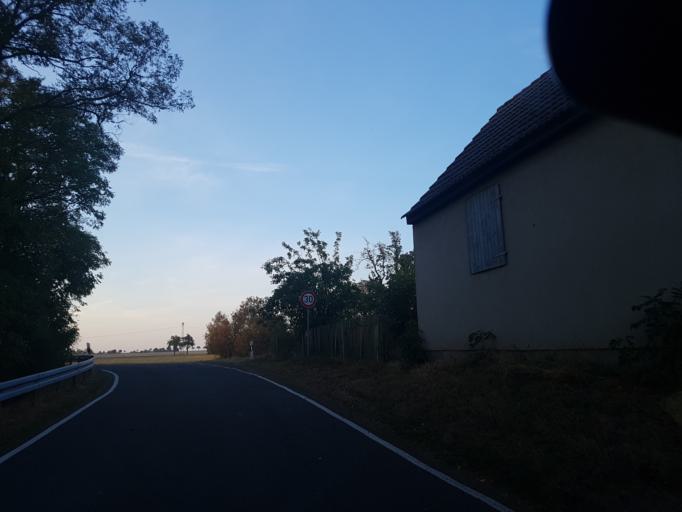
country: DE
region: Saxony
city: Stauchitz
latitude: 51.2898
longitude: 13.1911
